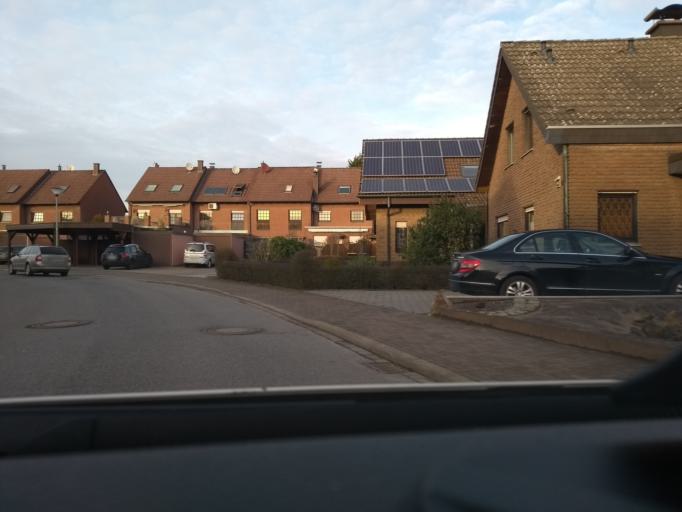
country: DE
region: North Rhine-Westphalia
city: Selm
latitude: 51.6983
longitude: 7.4535
